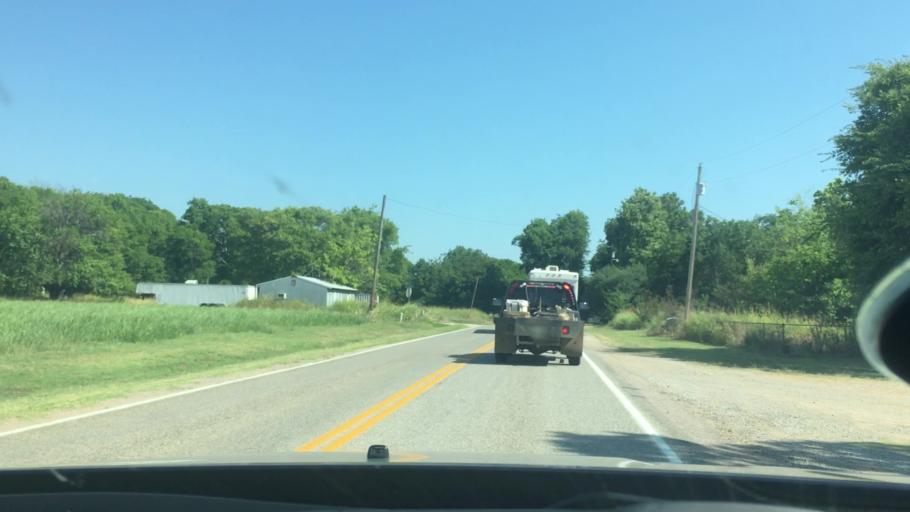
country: US
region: Oklahoma
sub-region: Johnston County
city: Tishomingo
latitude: 34.2017
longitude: -96.5428
